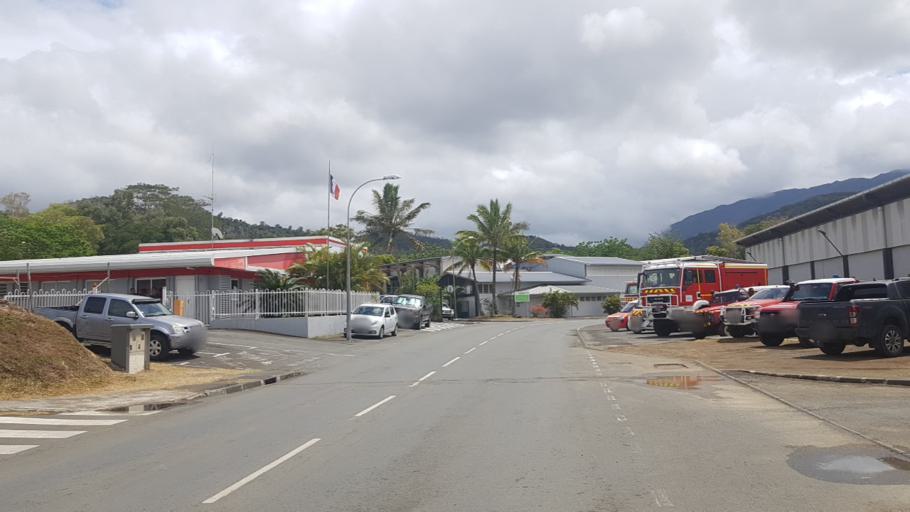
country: NC
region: South Province
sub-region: Dumbea
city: Dumbea
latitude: -22.2067
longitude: 166.4756
